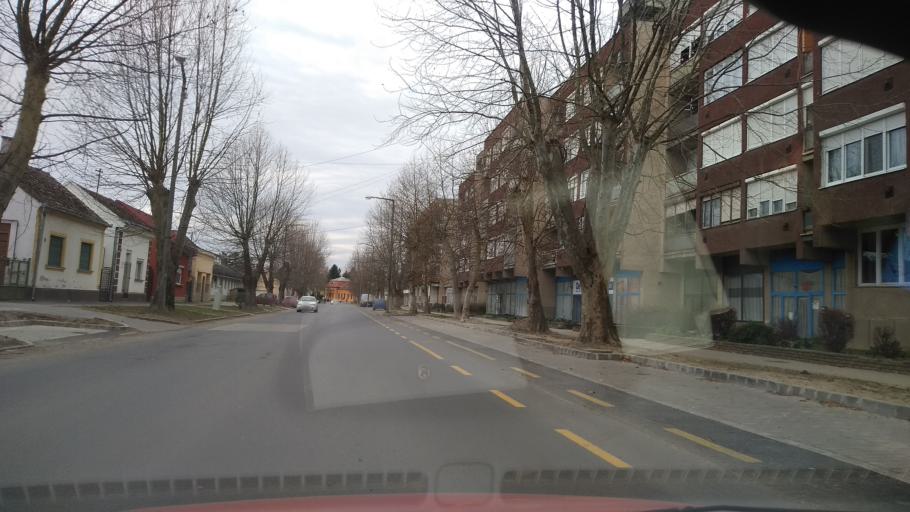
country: HU
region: Somogy
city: Barcs
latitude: 45.9590
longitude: 17.4573
